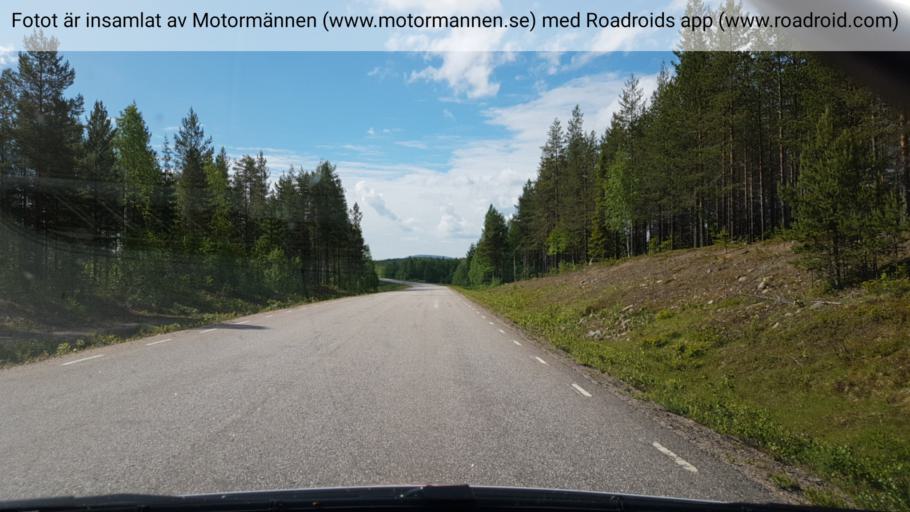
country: FI
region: Lapland
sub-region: Torniolaakso
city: Pello
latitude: 66.7458
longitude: 23.8670
